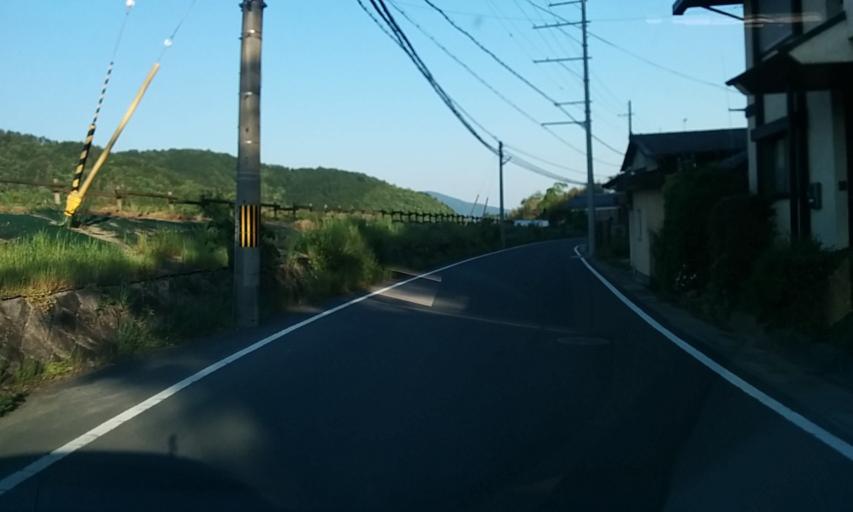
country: JP
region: Kyoto
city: Kameoka
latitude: 35.0874
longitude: 135.5132
